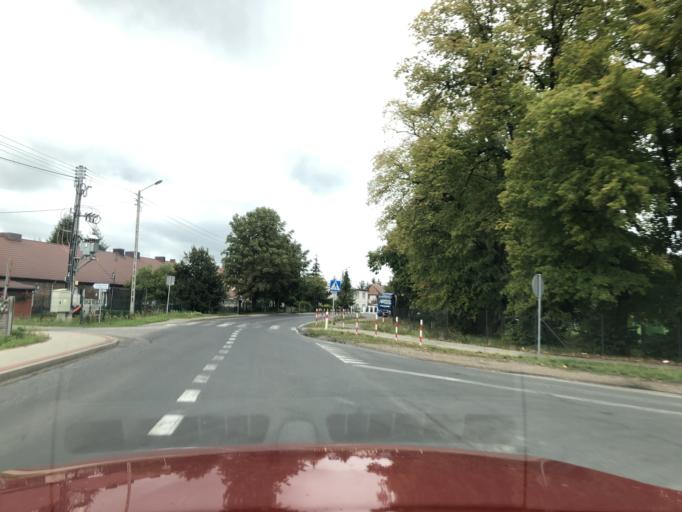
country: PL
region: Greater Poland Voivodeship
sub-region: Powiat szamotulski
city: Wronki
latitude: 52.6909
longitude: 16.3890
